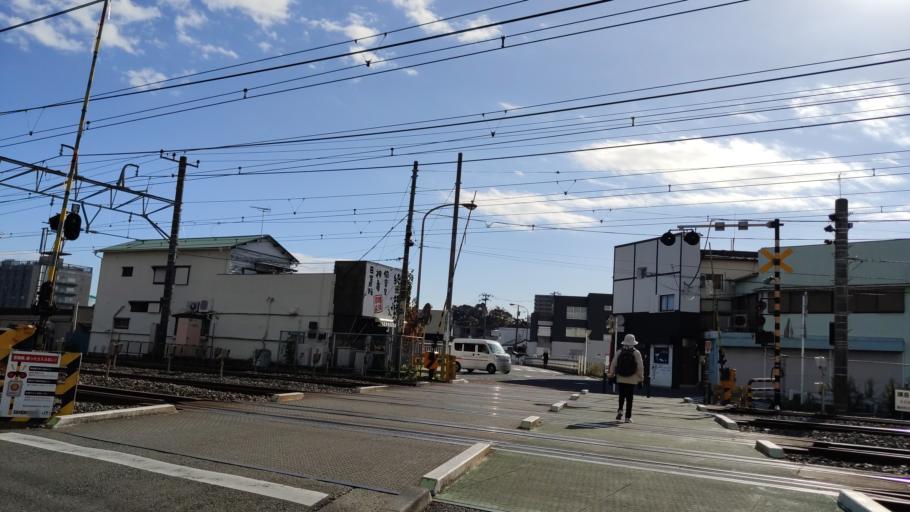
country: JP
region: Kanagawa
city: Fujisawa
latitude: 35.3371
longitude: 139.4962
